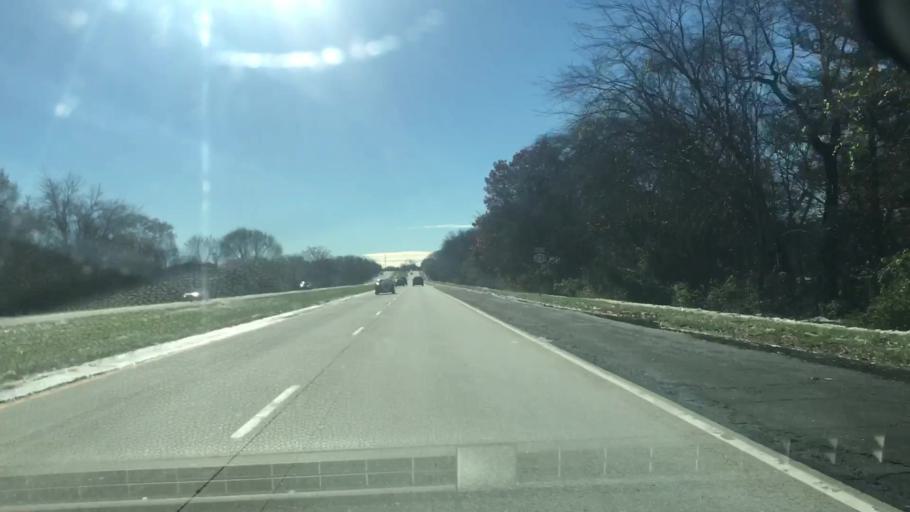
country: US
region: New York
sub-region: Suffolk County
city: North Babylon
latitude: 40.7127
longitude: -73.3142
